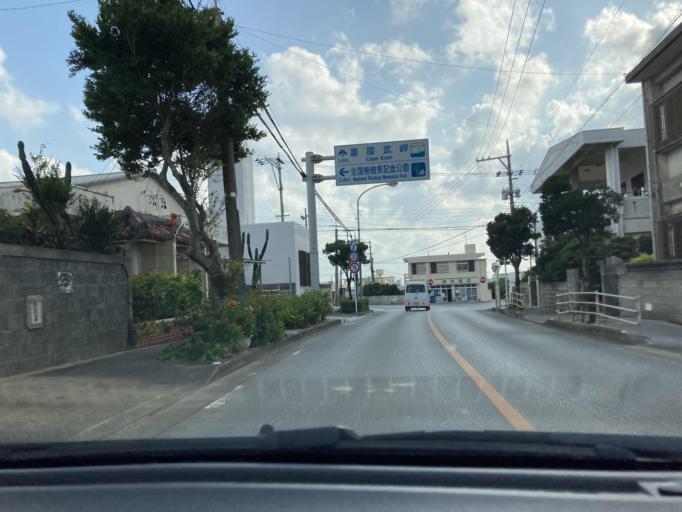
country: JP
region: Okinawa
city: Itoman
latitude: 26.0929
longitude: 127.6637
